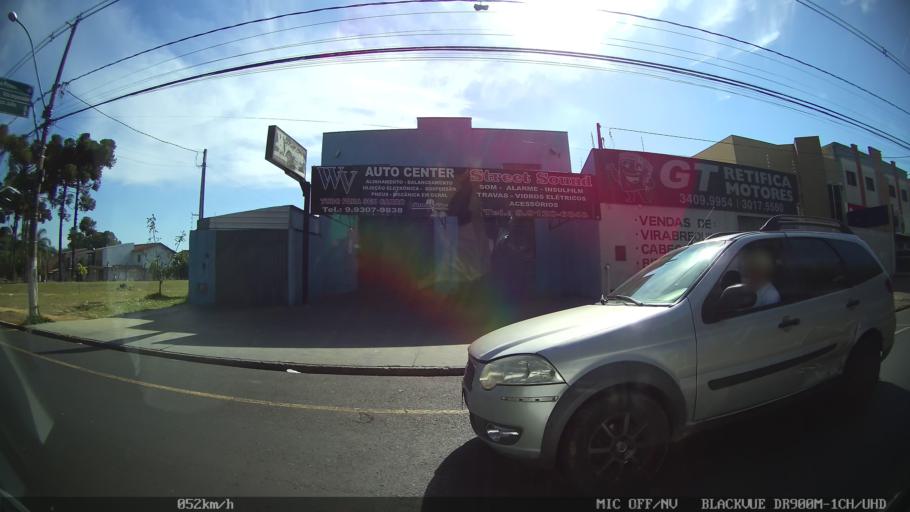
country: BR
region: Sao Paulo
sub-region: Franca
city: Franca
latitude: -20.5110
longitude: -47.4025
